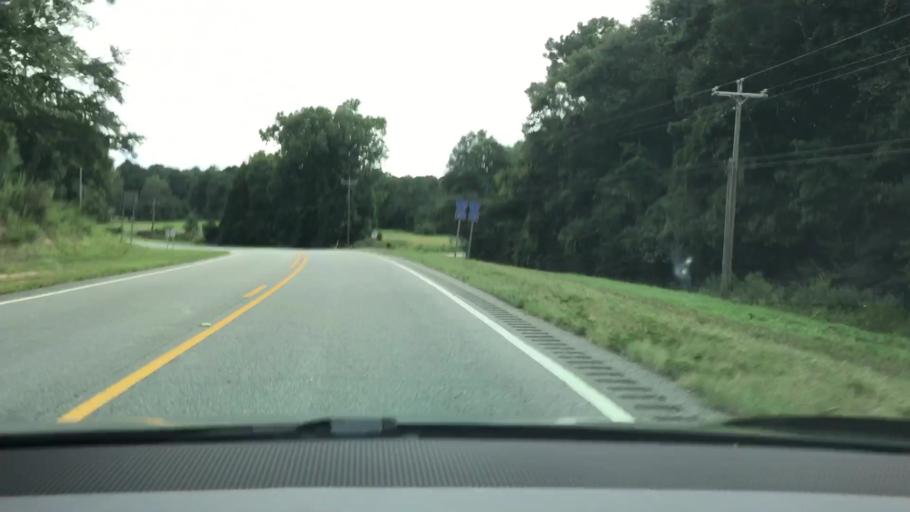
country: US
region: Alabama
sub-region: Coffee County
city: Elba
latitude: 31.5979
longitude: -86.0056
